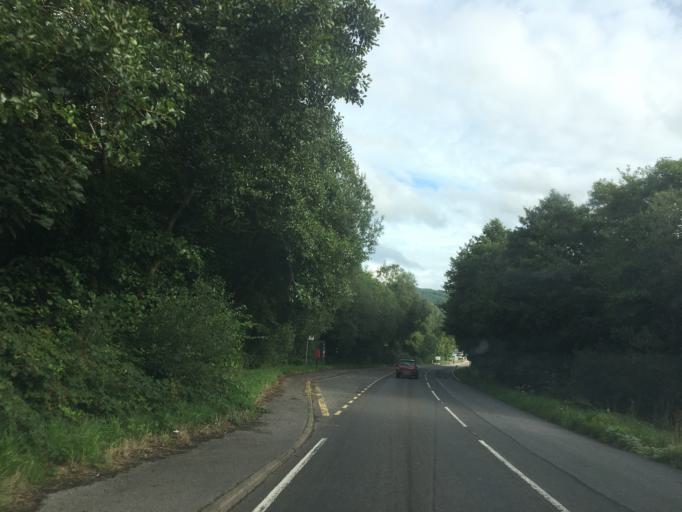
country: GB
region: Scotland
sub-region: Argyll and Bute
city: Oban
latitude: 56.3746
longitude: -5.4414
